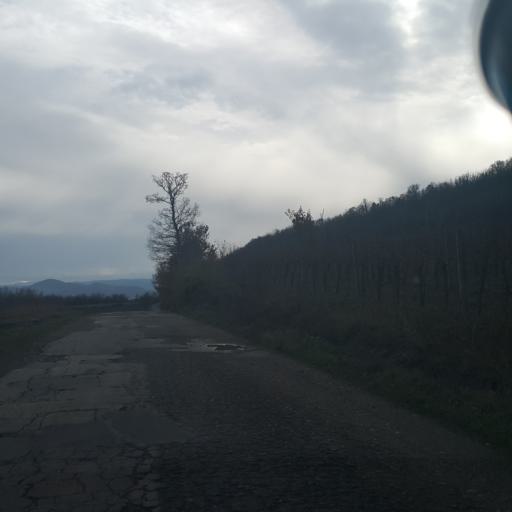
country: RS
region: Central Serbia
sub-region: Zajecarski Okrug
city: Knjazevac
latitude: 43.6141
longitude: 22.2607
